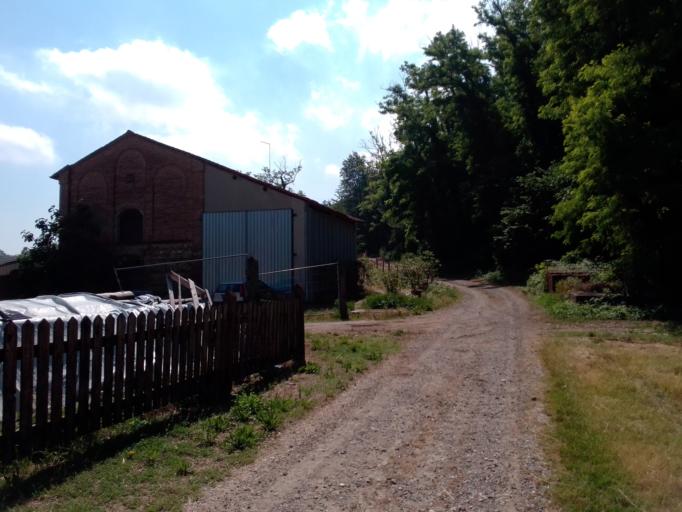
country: IT
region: Emilia-Romagna
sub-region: Provincia di Piacenza
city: Borgonovo Valtidone
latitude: 44.9841
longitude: 9.4725
